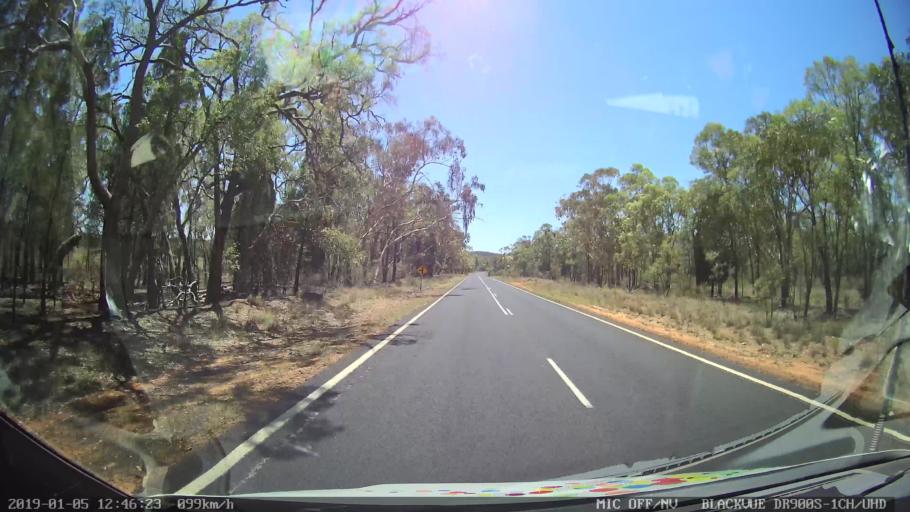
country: AU
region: New South Wales
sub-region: Warrumbungle Shire
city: Coonabarabran
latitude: -31.1185
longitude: 149.5618
